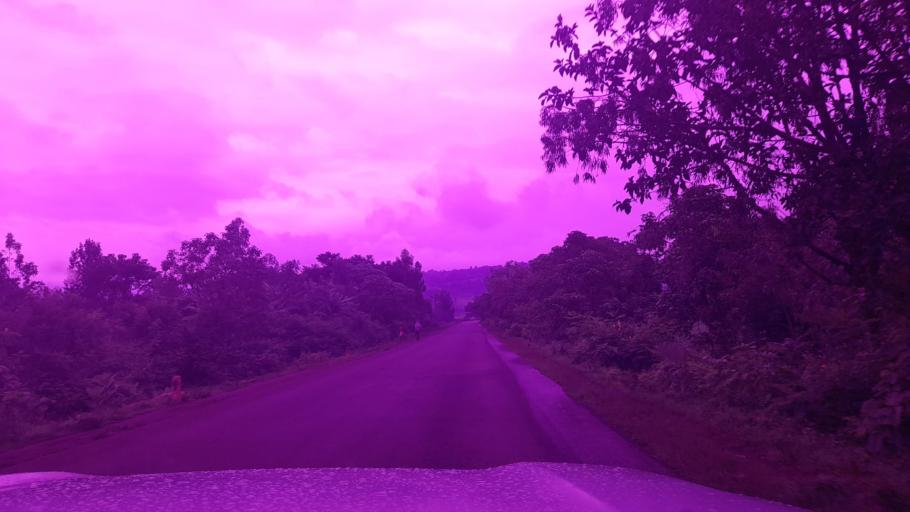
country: ET
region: Oromiya
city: Jima
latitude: 7.6876
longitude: 37.2423
